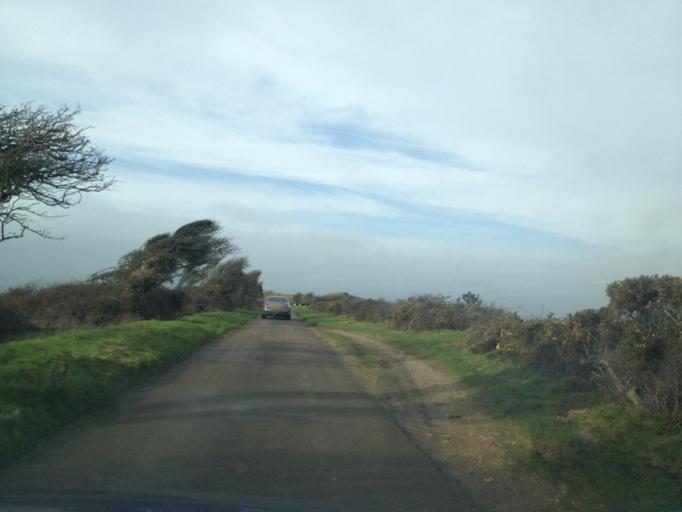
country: GB
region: England
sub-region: Isle of Wight
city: Brading
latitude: 50.6694
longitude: -1.1145
